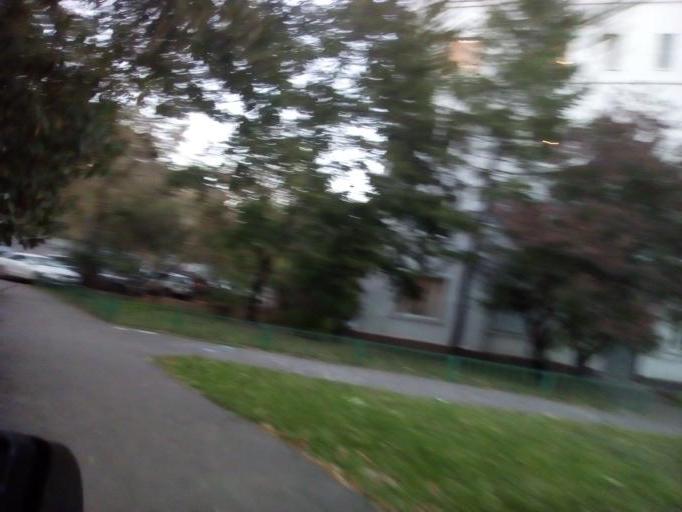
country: RU
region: Moscow
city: Sokol
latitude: 55.8064
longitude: 37.4997
